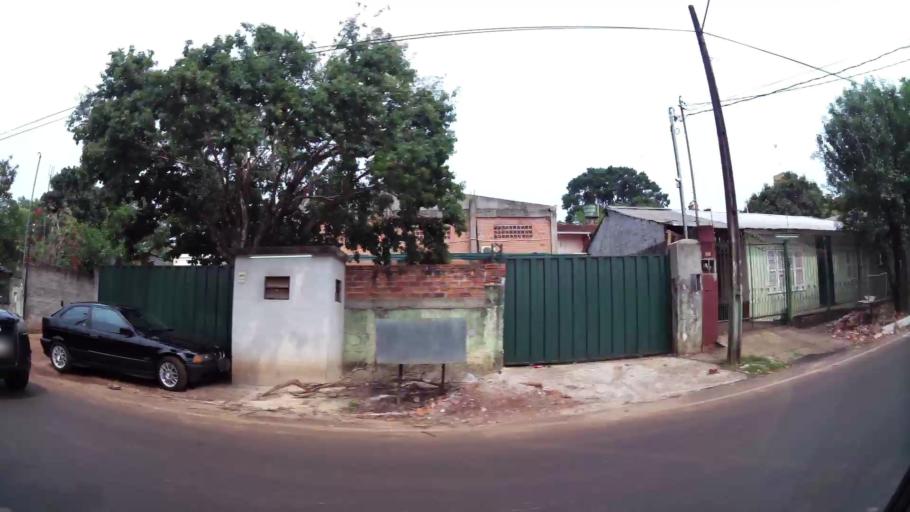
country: BR
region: Parana
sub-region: Foz Do Iguacu
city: Foz do Iguacu
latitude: -25.5524
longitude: -54.6065
